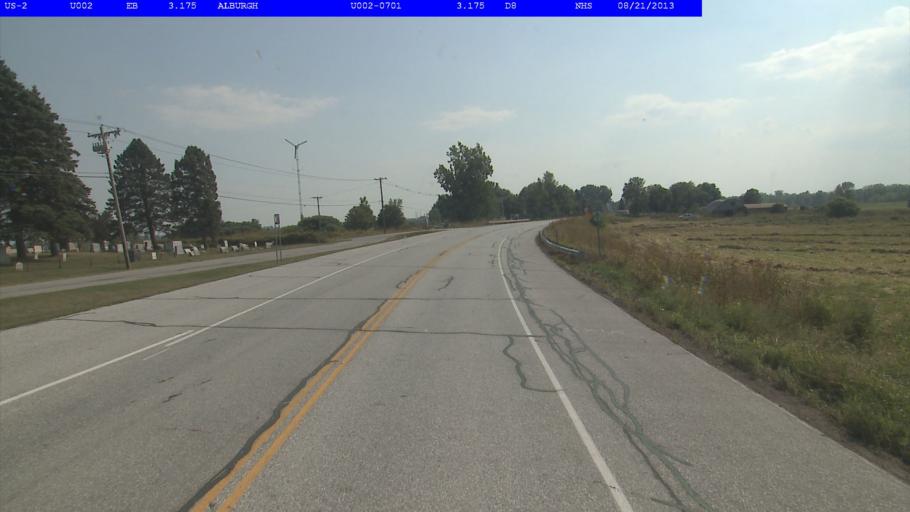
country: US
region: New York
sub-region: Clinton County
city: Rouses Point
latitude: 44.9881
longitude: -73.2961
